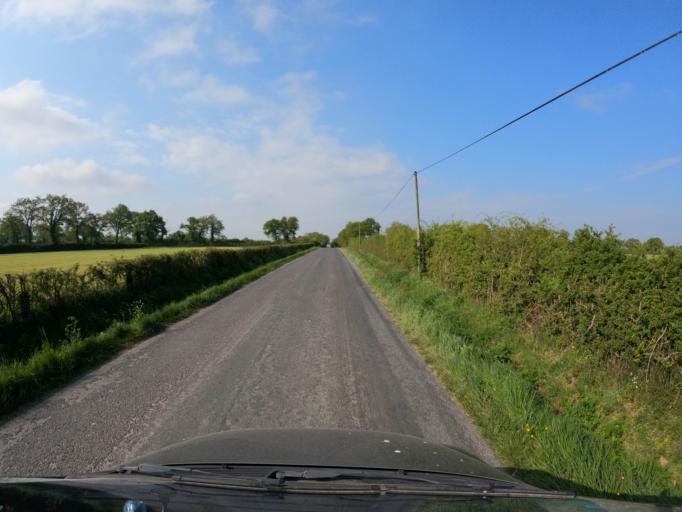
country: FR
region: Pays de la Loire
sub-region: Departement de Maine-et-Loire
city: Torfou
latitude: 47.0500
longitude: -1.0970
